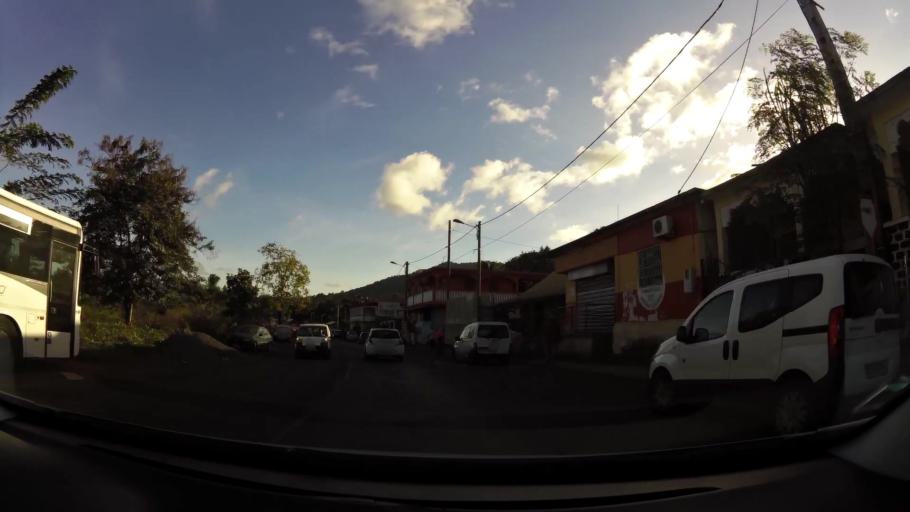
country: YT
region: Mamoudzou
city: Mamoudzou
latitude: -12.8076
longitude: 45.2048
